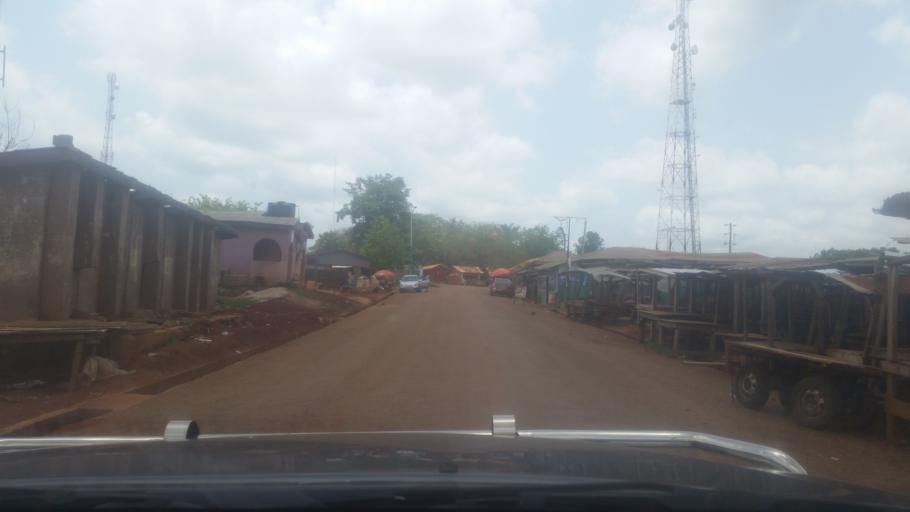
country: GH
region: Western
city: Bibiani
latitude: 6.8059
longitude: -2.5180
